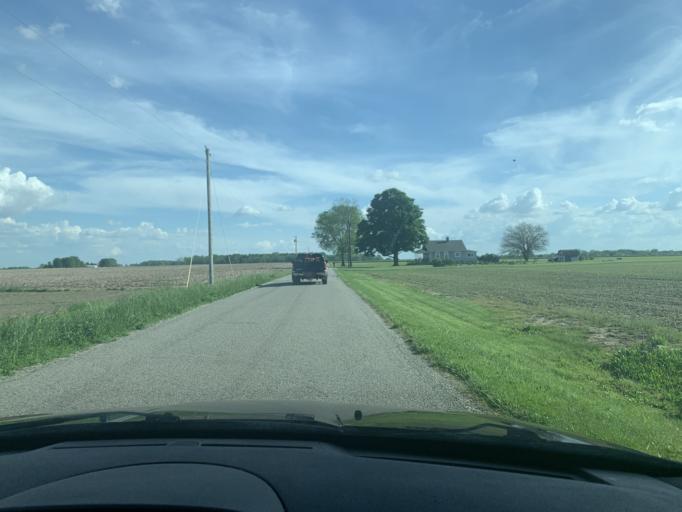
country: US
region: Ohio
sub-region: Logan County
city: De Graff
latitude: 40.2505
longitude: -84.0171
